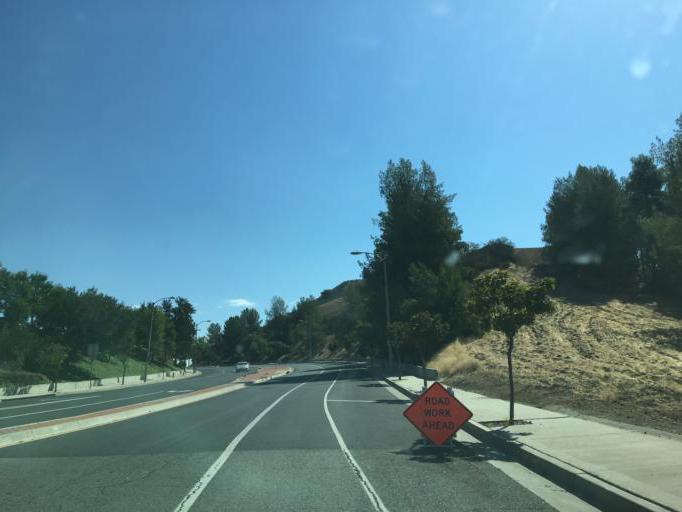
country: US
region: California
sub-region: Los Angeles County
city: Agoura
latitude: 34.1364
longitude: -118.7241
